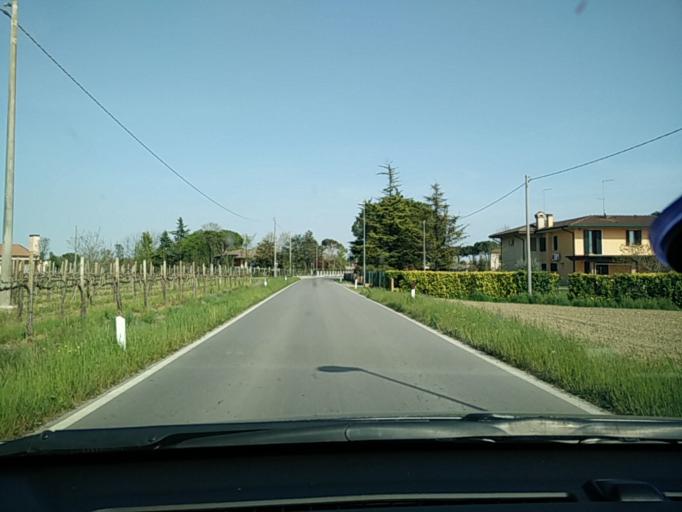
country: IT
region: Veneto
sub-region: Provincia di Venezia
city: Ceggia
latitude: 45.6876
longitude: 12.6253
